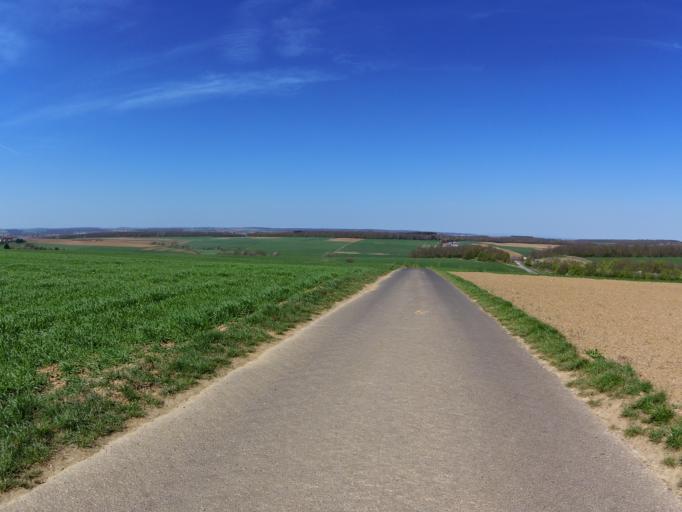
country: DE
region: Bavaria
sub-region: Regierungsbezirk Unterfranken
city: Rottendorf
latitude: 49.7947
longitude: 10.0502
